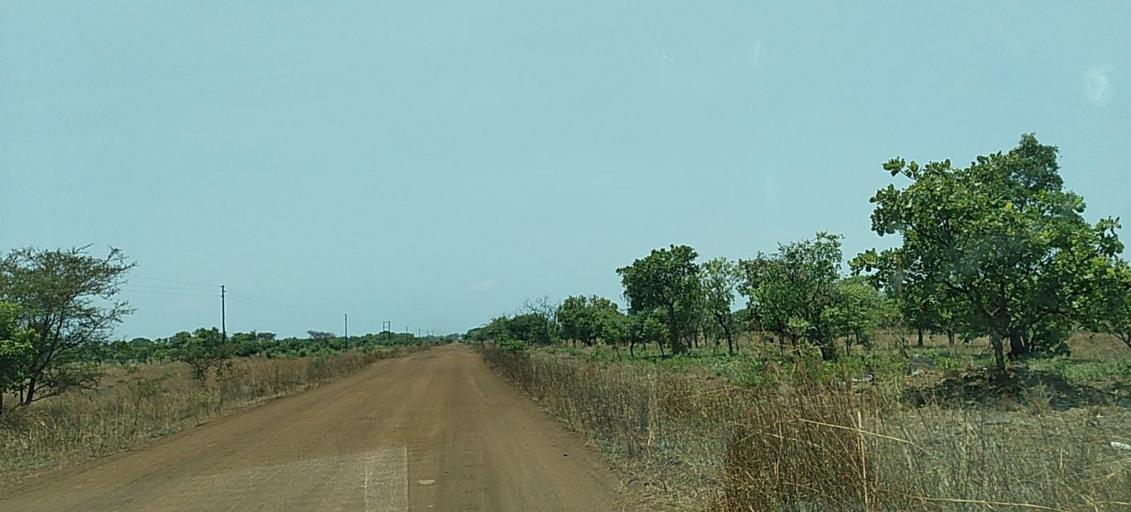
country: ZM
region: Copperbelt
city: Mpongwe
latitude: -13.7140
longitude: 27.8684
